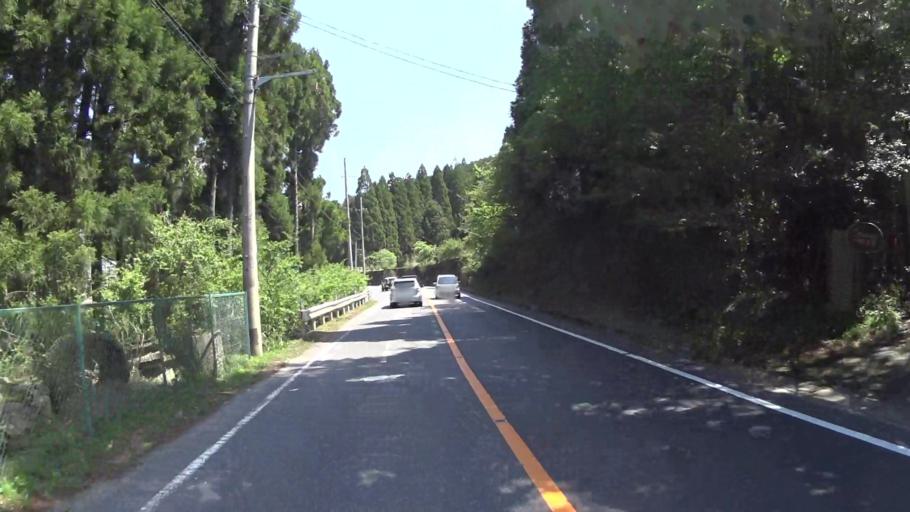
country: JP
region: Shiga Prefecture
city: Kitahama
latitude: 35.1503
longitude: 135.8445
